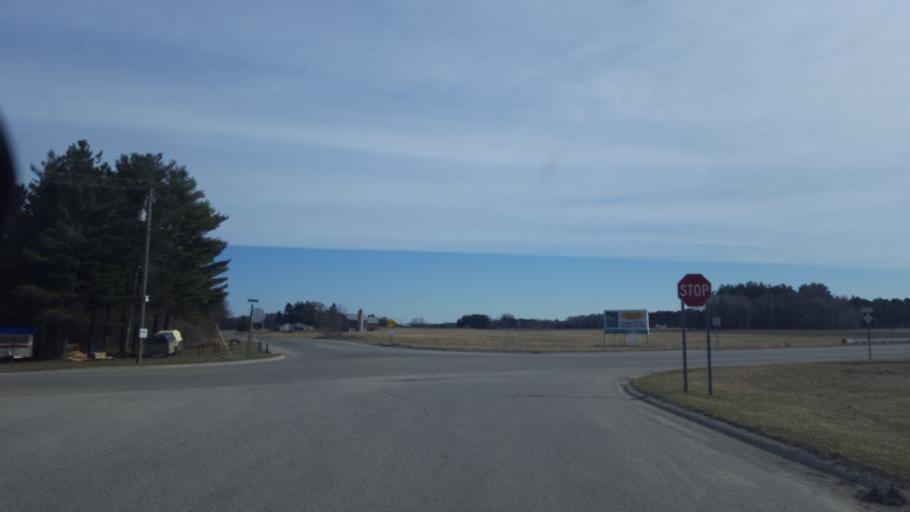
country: US
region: Michigan
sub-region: Mecosta County
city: Big Rapids
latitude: 43.5836
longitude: -85.4991
